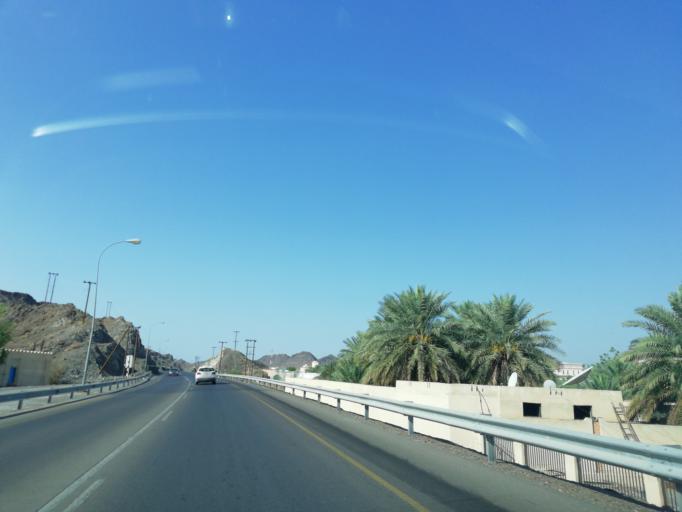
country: OM
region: Ash Sharqiyah
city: Ibra'
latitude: 22.8340
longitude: 58.1718
